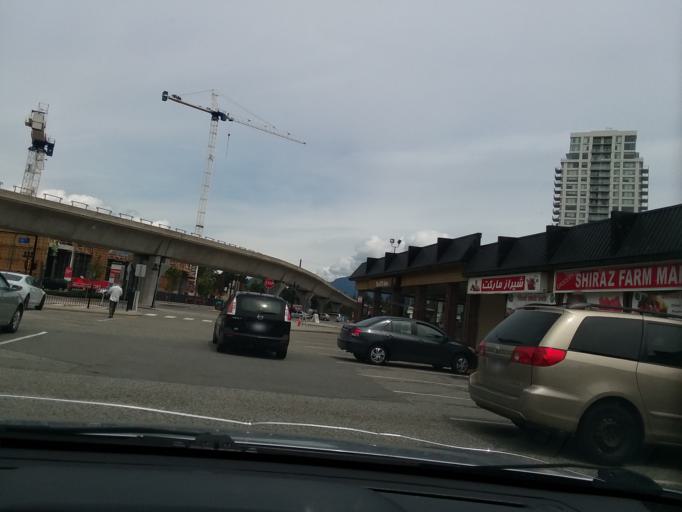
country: CA
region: British Columbia
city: Port Moody
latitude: 49.2612
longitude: -122.8892
